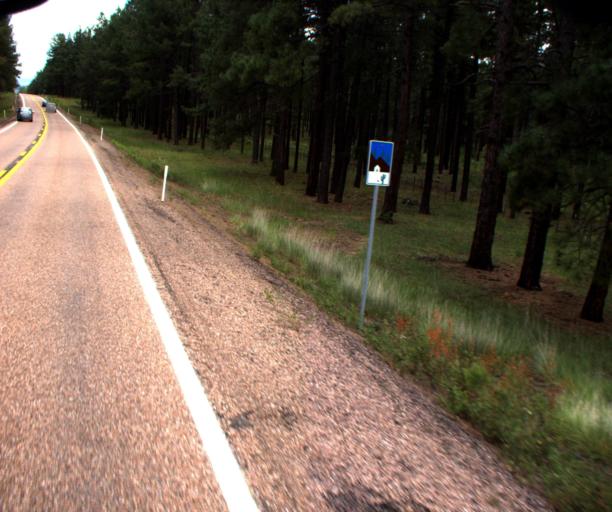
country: US
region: Arizona
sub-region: Navajo County
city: Pinetop-Lakeside
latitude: 34.0644
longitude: -109.7749
